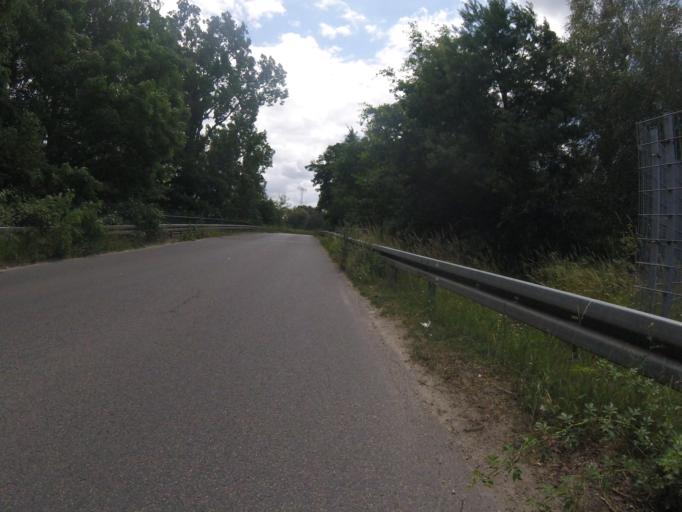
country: DE
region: Brandenburg
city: Mittenwalde
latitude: 52.2518
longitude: 13.5222
